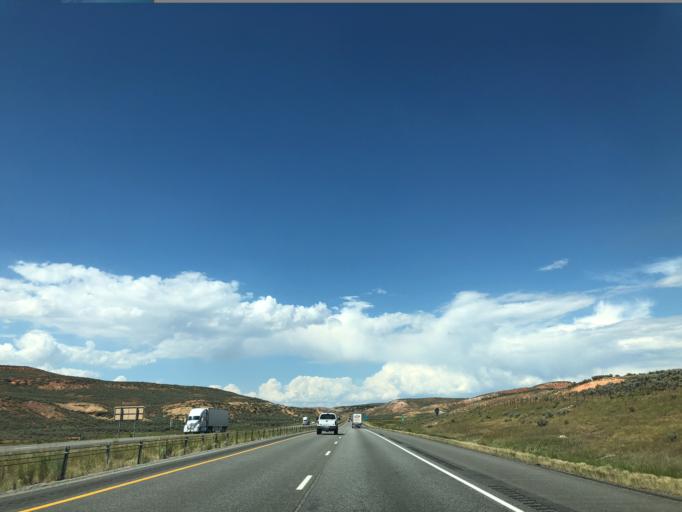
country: US
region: Wyoming
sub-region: Uinta County
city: Evanston
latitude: 41.1419
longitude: -111.1507
